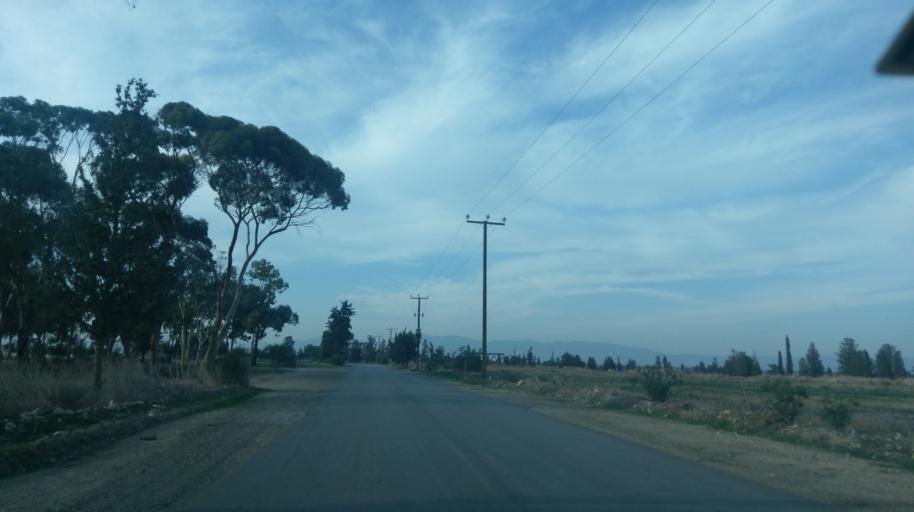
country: CY
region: Larnaka
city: Pergamos
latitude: 35.1225
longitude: 33.6673
